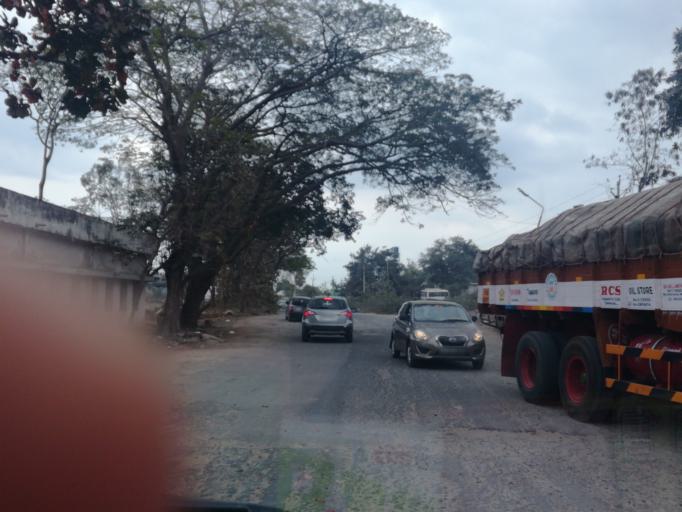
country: IN
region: Andhra Pradesh
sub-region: Chittoor
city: Ramapuram
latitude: 13.0894
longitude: 79.1342
